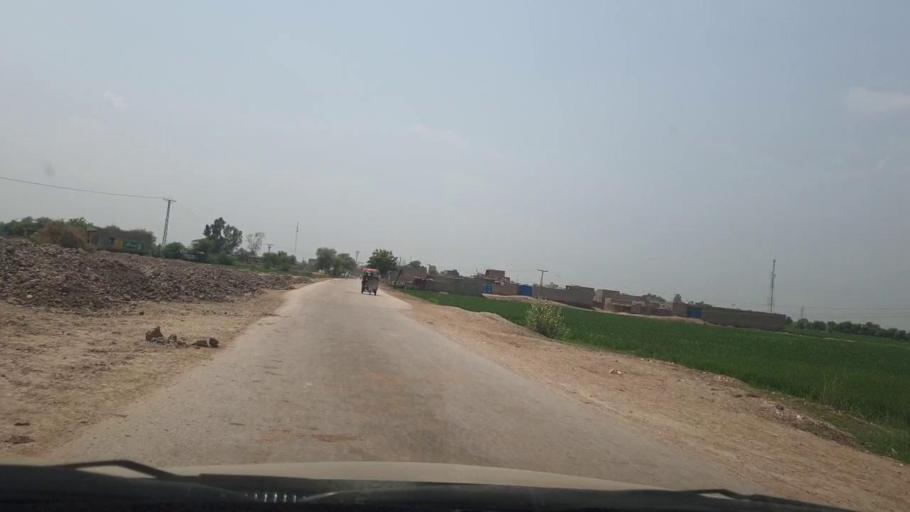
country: PK
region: Sindh
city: Ratodero
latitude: 27.7326
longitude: 68.2845
